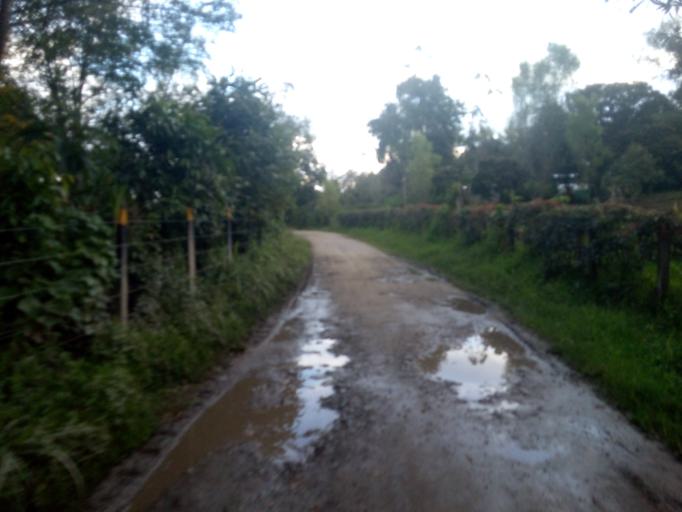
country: CO
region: Cundinamarca
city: Tenza
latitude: 5.1084
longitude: -73.4159
